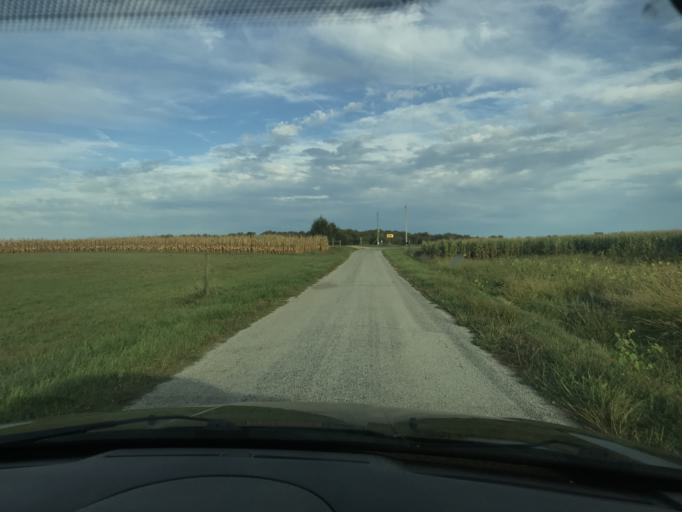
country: US
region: Ohio
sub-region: Logan County
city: West Liberty
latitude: 40.2028
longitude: -83.8081
